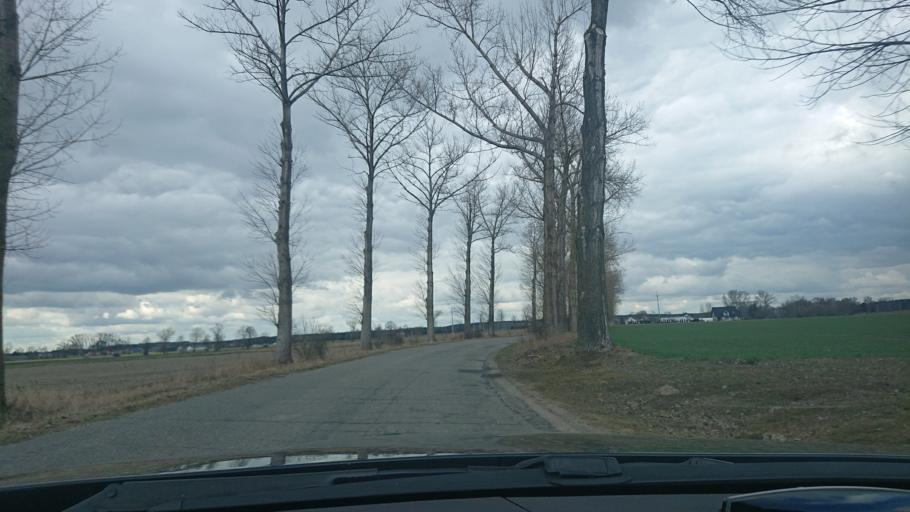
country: PL
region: Greater Poland Voivodeship
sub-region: Powiat gnieznienski
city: Niechanowo
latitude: 52.5848
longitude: 17.7011
